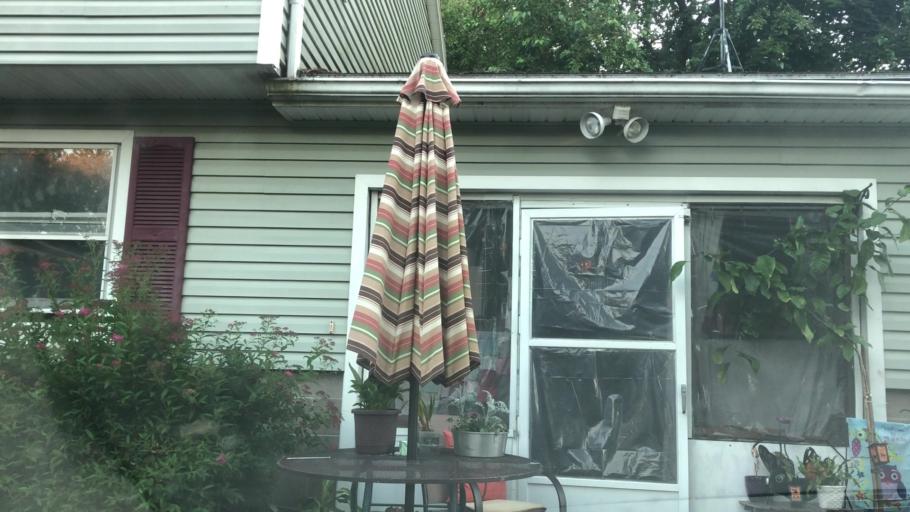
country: US
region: New York
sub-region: Wayne County
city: Macedon
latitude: 43.1273
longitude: -77.3088
